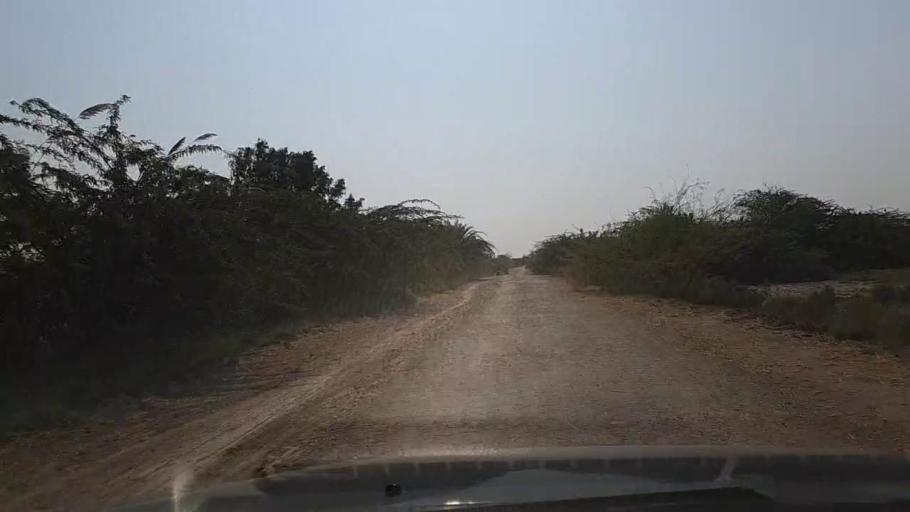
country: PK
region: Sindh
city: Mirpur Sakro
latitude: 24.3948
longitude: 67.6658
